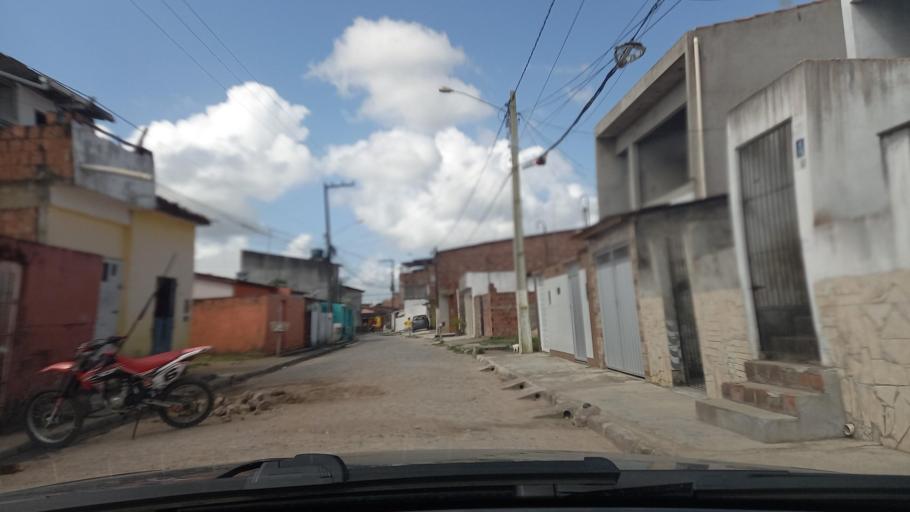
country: BR
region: Pernambuco
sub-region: Goiana
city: Goiana
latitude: -7.5655
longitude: -35.0168
